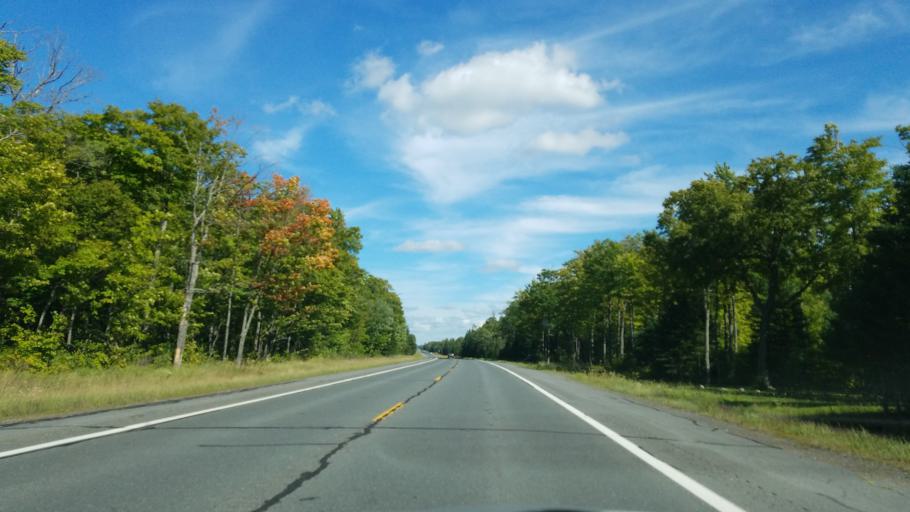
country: US
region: Michigan
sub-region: Baraga County
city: L'Anse
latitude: 46.5789
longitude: -88.4491
